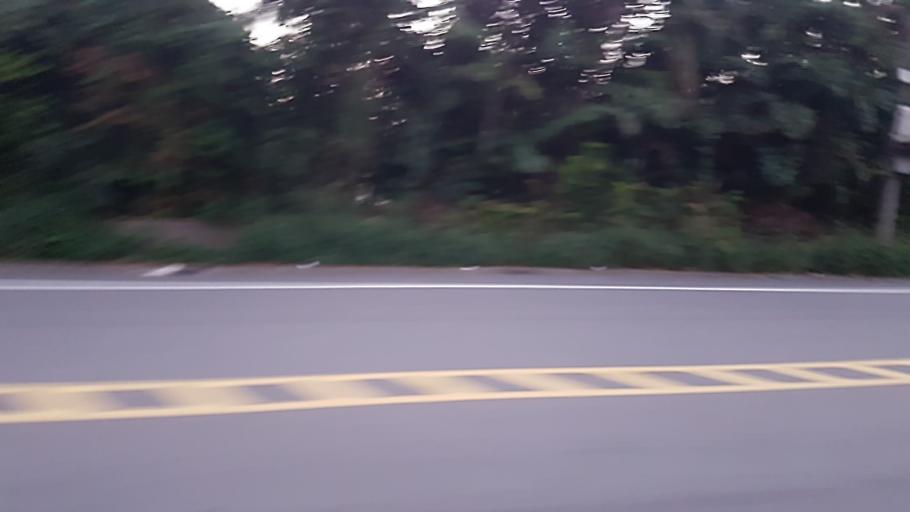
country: TW
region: Taiwan
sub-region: Hsinchu
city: Hsinchu
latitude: 24.7663
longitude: 120.9634
